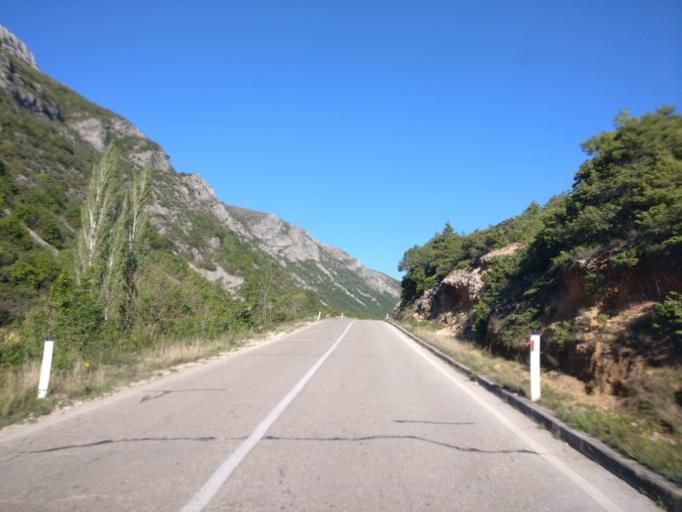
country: BA
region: Federation of Bosnia and Herzegovina
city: Stolac
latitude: 43.0759
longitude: 18.0266
